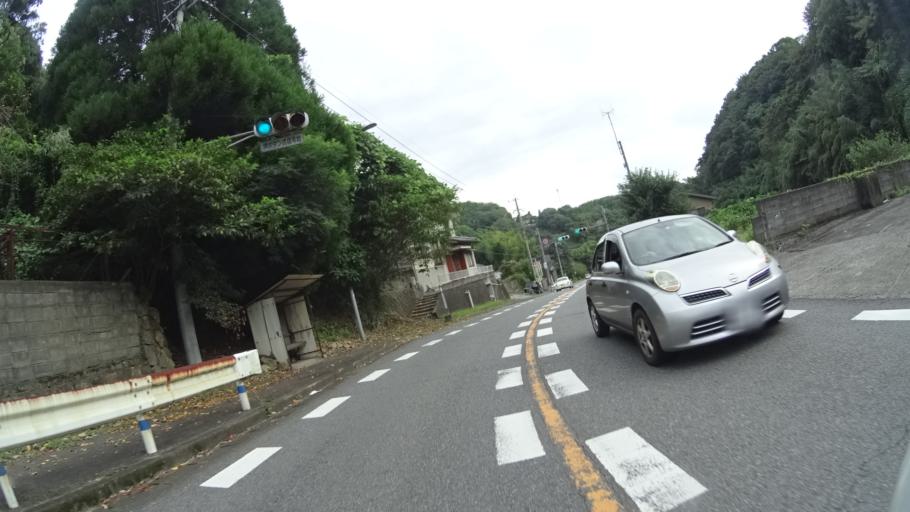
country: JP
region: Oita
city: Beppu
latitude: 33.3262
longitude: 131.4747
